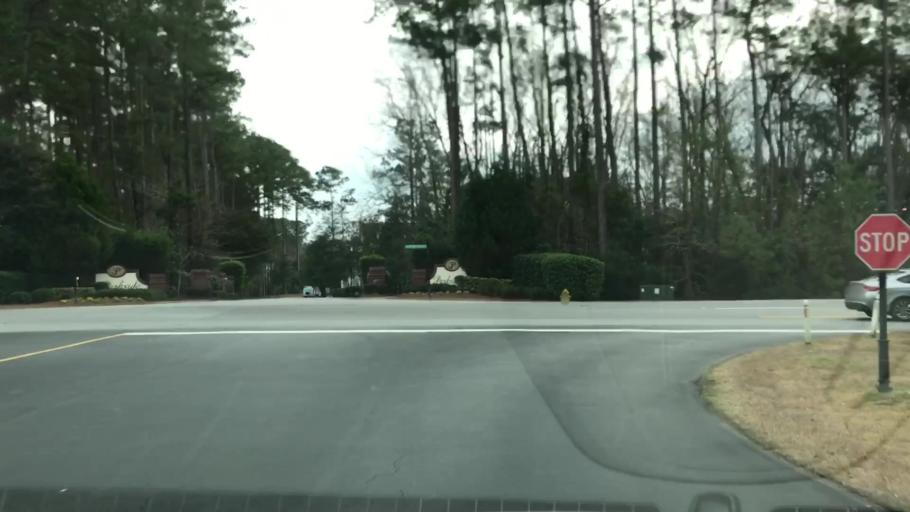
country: US
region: South Carolina
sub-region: Beaufort County
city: Bluffton
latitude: 32.2758
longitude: -80.9277
